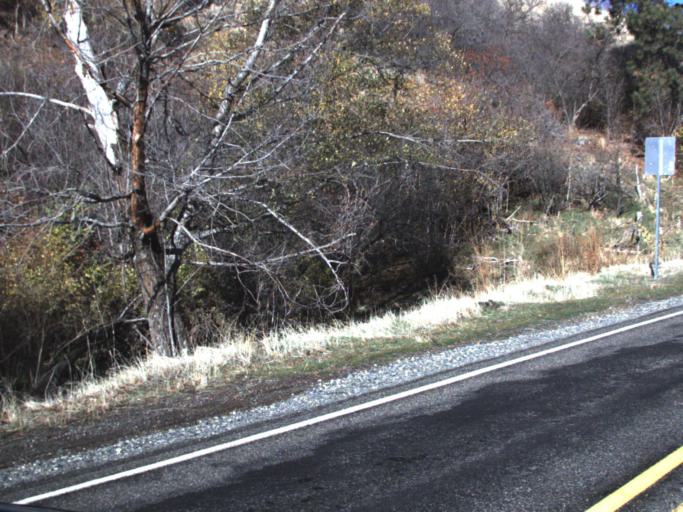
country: US
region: Washington
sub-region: Asotin County
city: Asotin
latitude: 46.0534
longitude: -117.2389
